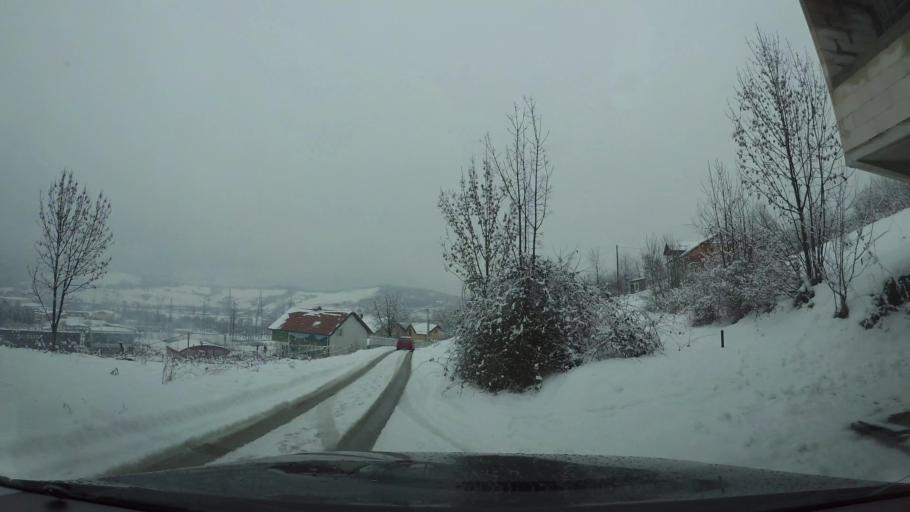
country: BA
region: Federation of Bosnia and Herzegovina
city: Vogosca
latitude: 43.8787
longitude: 18.3175
